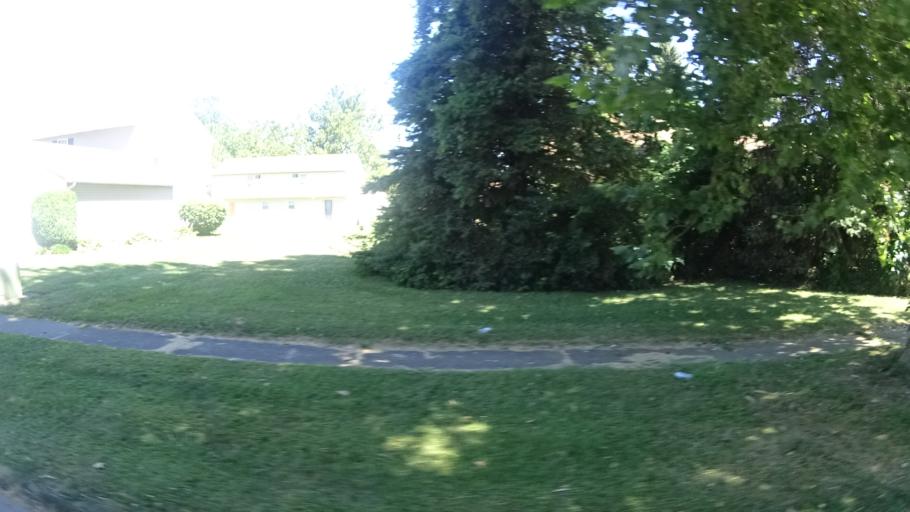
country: US
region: Ohio
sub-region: Erie County
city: Sandusky
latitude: 41.4328
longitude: -82.6705
